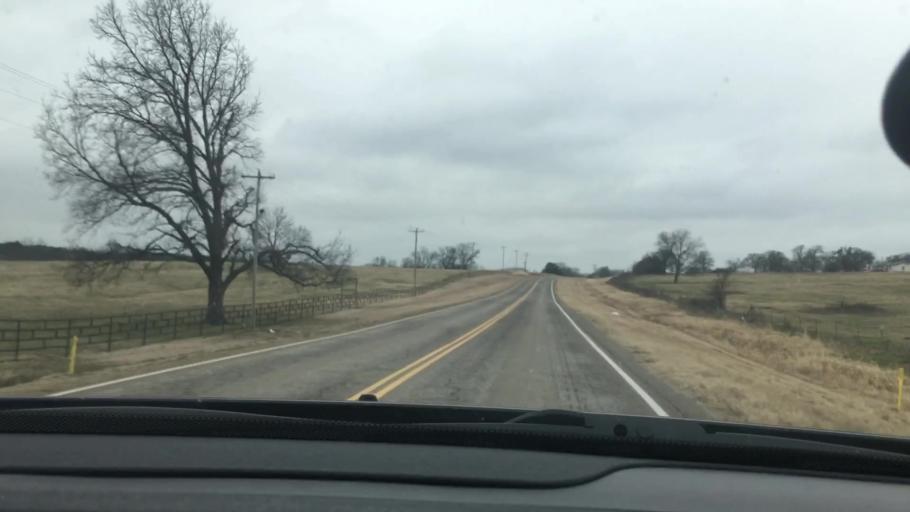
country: US
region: Oklahoma
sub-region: Carter County
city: Dickson
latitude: 34.2081
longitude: -96.9768
